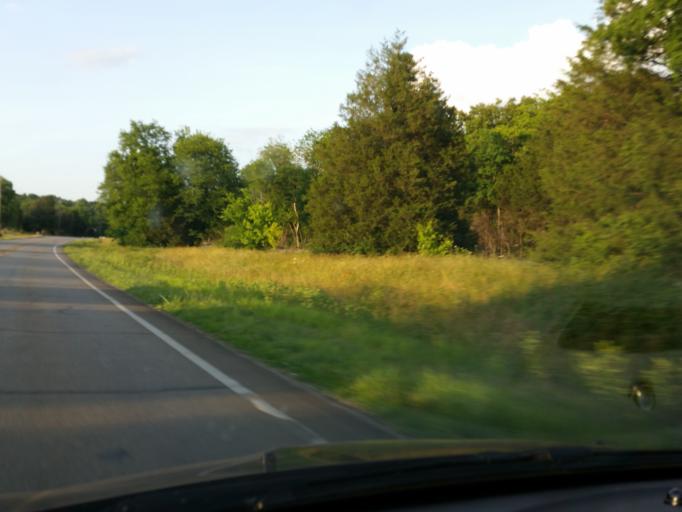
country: US
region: Georgia
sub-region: Dade County
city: Trenton
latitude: 34.9387
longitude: -85.4521
